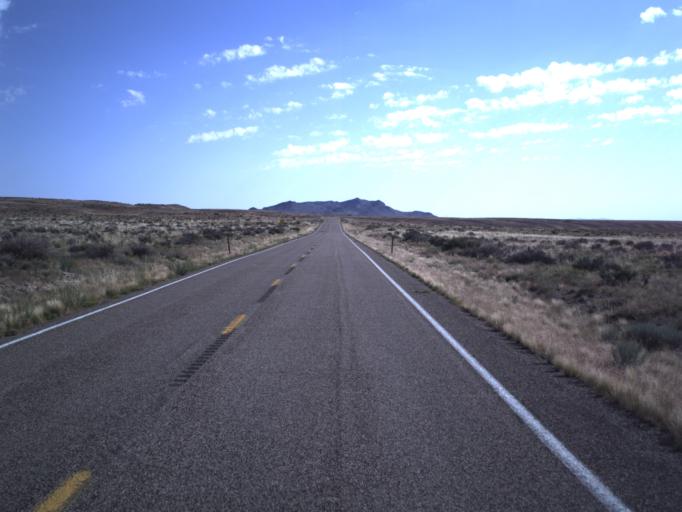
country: US
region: Utah
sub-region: Beaver County
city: Milford
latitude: 38.7575
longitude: -112.9441
